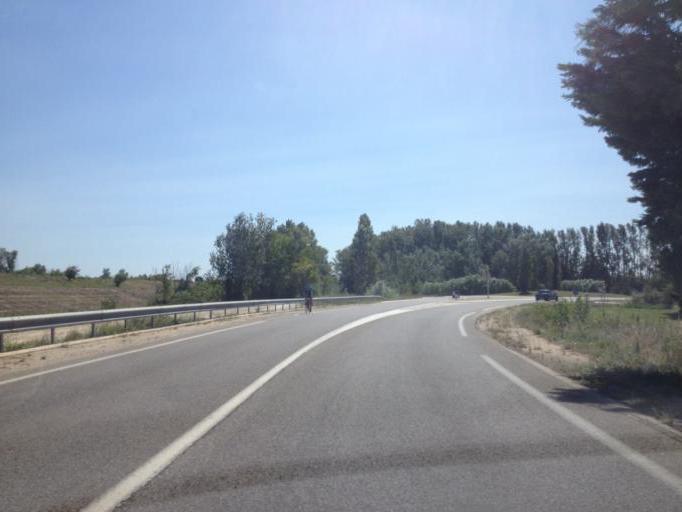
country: FR
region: Languedoc-Roussillon
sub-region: Departement du Gard
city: Roquemaure
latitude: 44.0457
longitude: 4.7931
